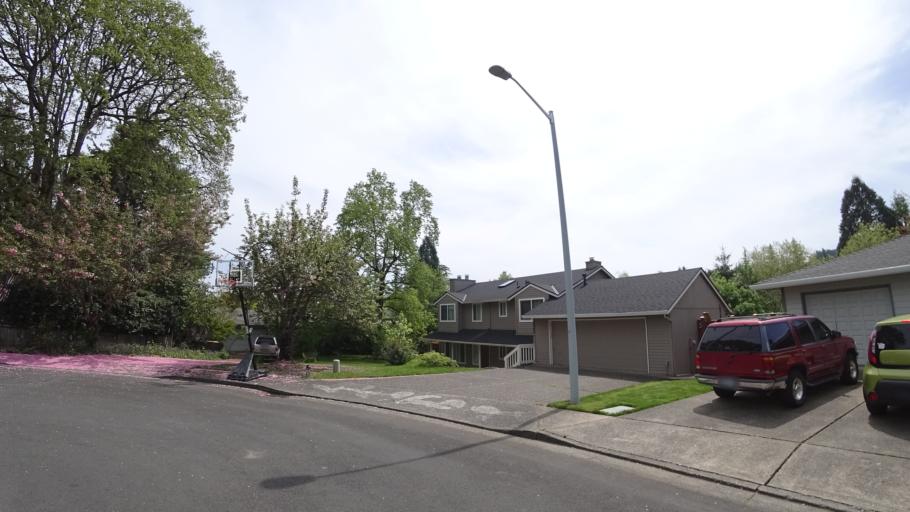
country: US
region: Oregon
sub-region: Washington County
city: Aloha
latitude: 45.4619
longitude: -122.8463
